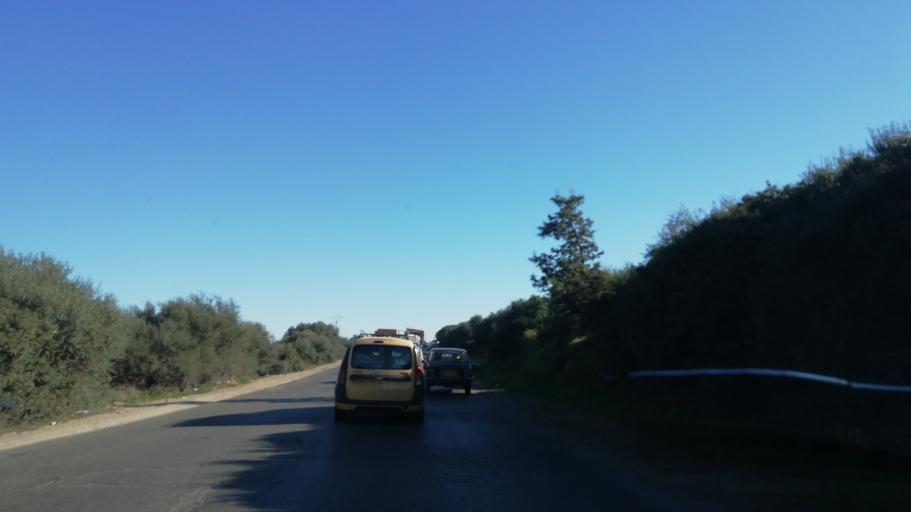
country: DZ
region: Relizane
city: Smala
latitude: 35.7009
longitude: 0.7760
